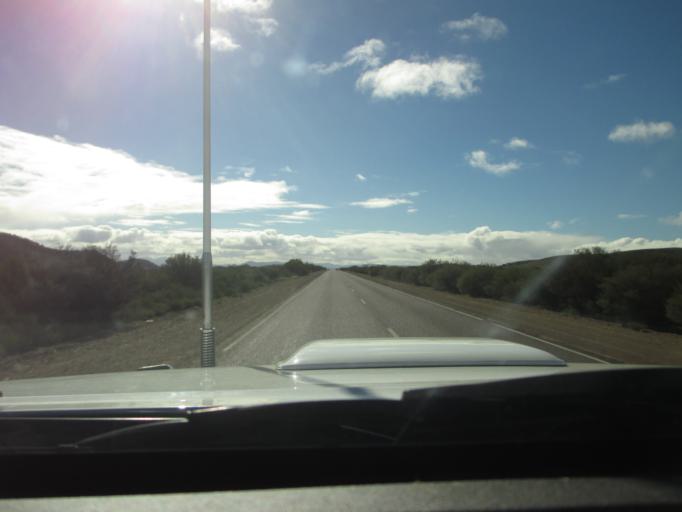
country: AU
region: South Australia
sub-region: Flinders Ranges
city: Quorn
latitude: -31.9323
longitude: 138.4149
